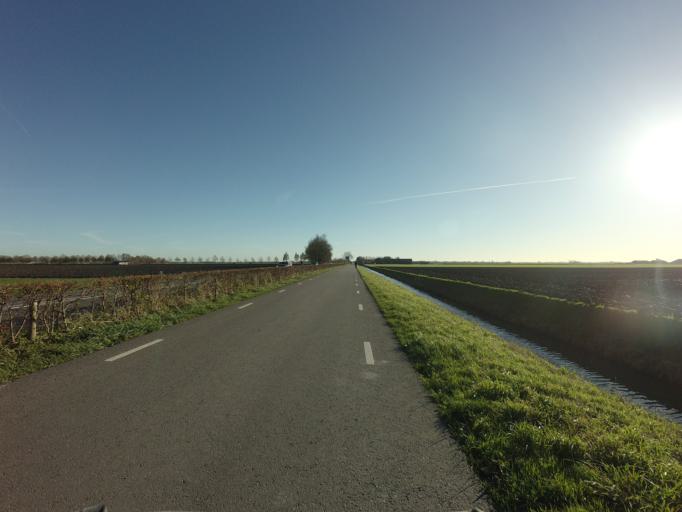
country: NL
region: South Holland
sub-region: Gemeente Nieuwkoop
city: Nieuwkoop
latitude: 52.1803
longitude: 4.7671
